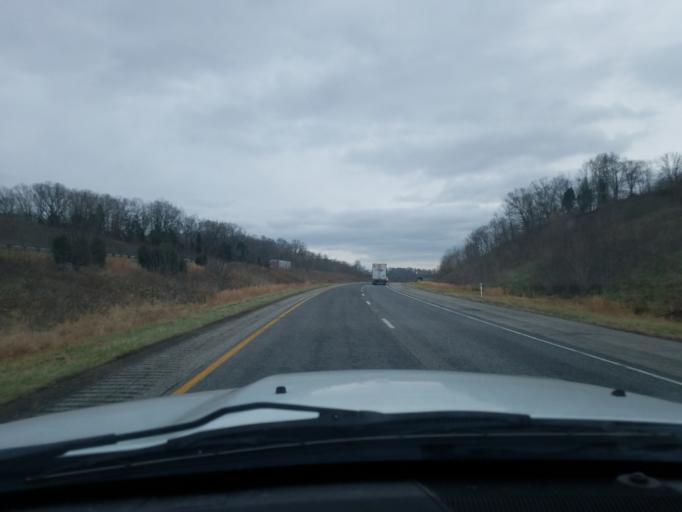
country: US
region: Indiana
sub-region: Dubois County
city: Ferdinand
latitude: 38.2070
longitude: -86.7960
